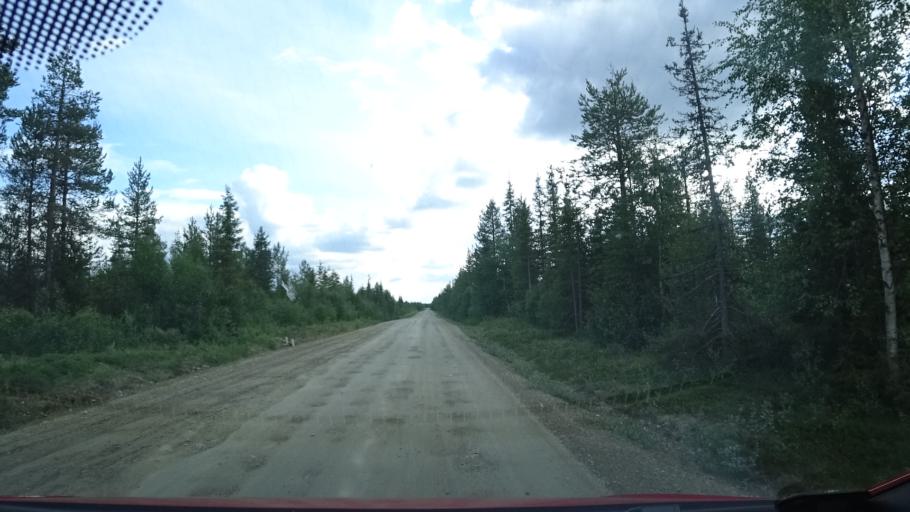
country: FI
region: Lapland
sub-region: Tunturi-Lappi
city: Kittilae
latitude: 68.0479
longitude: 25.2728
